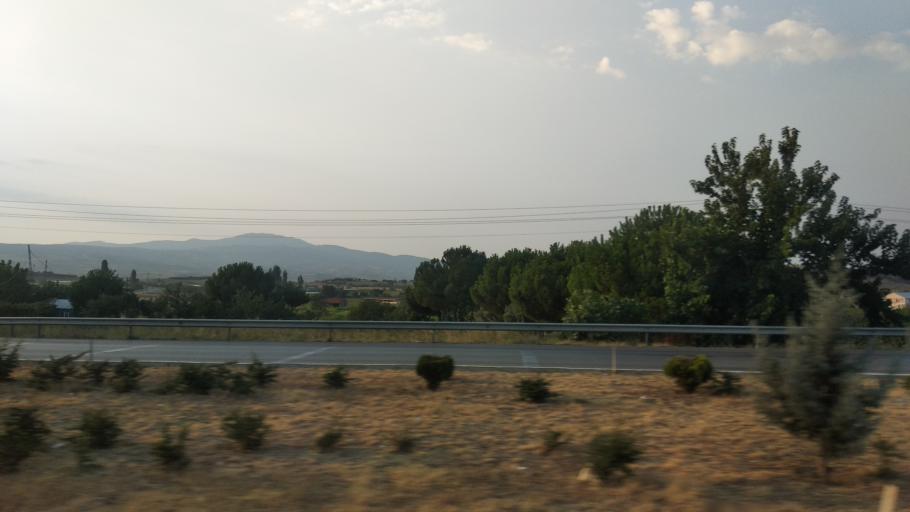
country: TR
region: Manisa
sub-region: Kula
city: Kula
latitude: 38.5506
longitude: 28.6795
